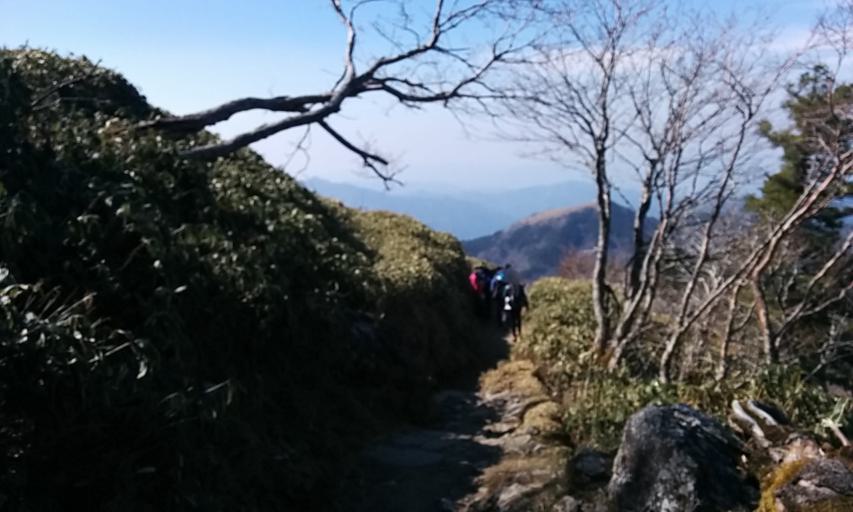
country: JP
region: Tokushima
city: Wakimachi
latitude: 33.8563
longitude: 134.0957
